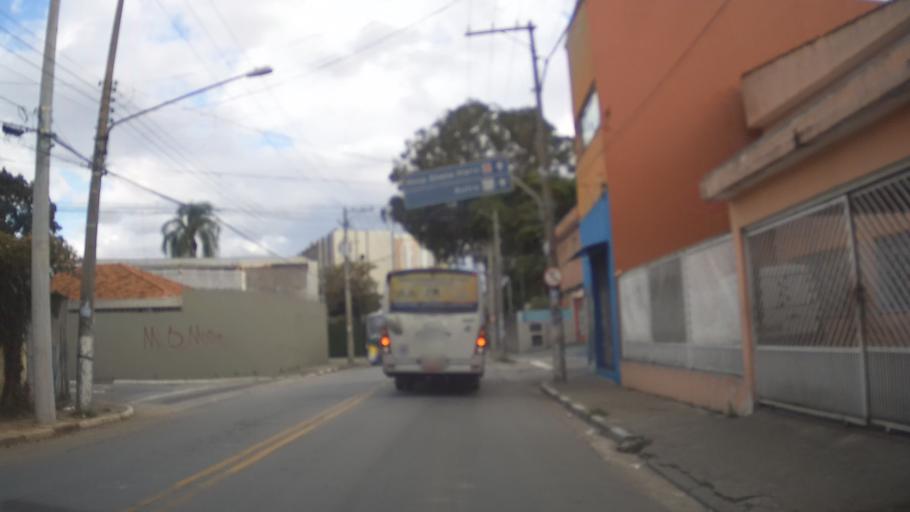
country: BR
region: Sao Paulo
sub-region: Guarulhos
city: Guarulhos
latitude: -23.4780
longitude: -46.5531
